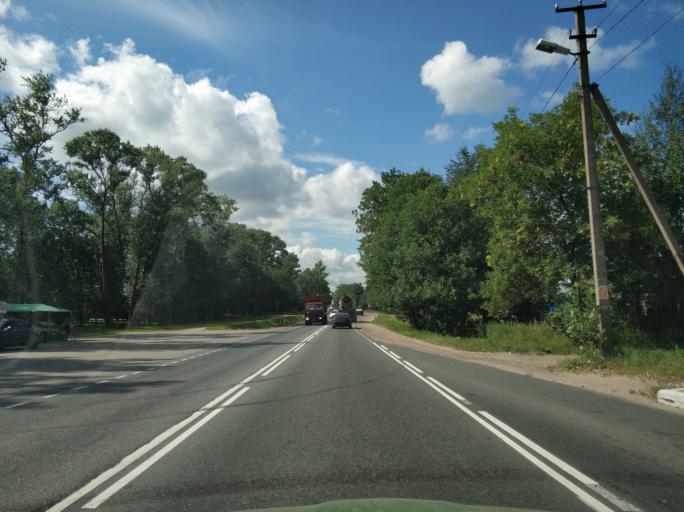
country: RU
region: Leningrad
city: Romanovka
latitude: 60.0486
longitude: 30.7073
